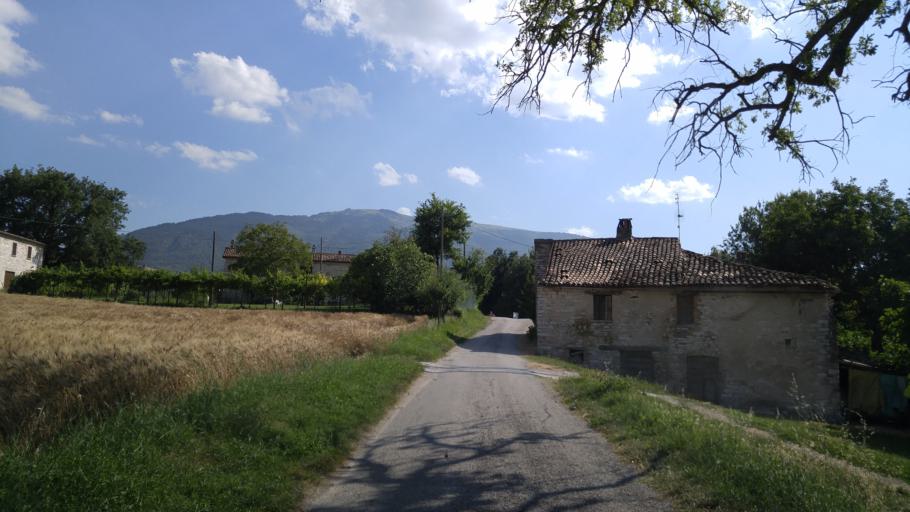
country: IT
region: The Marches
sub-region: Provincia di Pesaro e Urbino
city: Canavaccio
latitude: 43.6893
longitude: 12.7312
